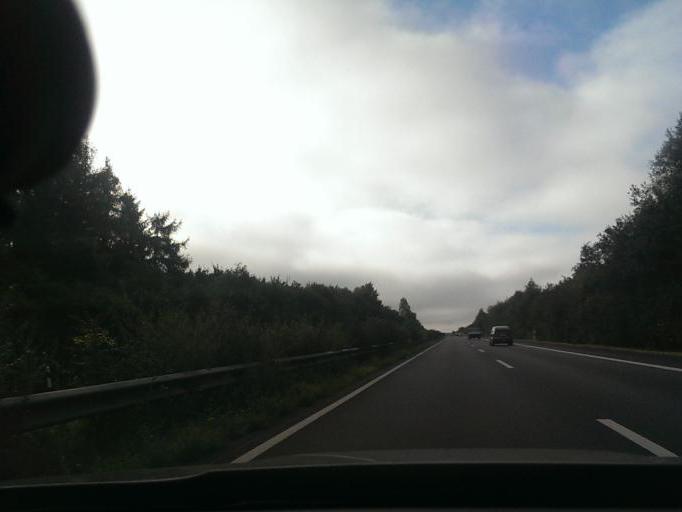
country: DE
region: Lower Saxony
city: Flothe
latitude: 52.1031
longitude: 10.4905
